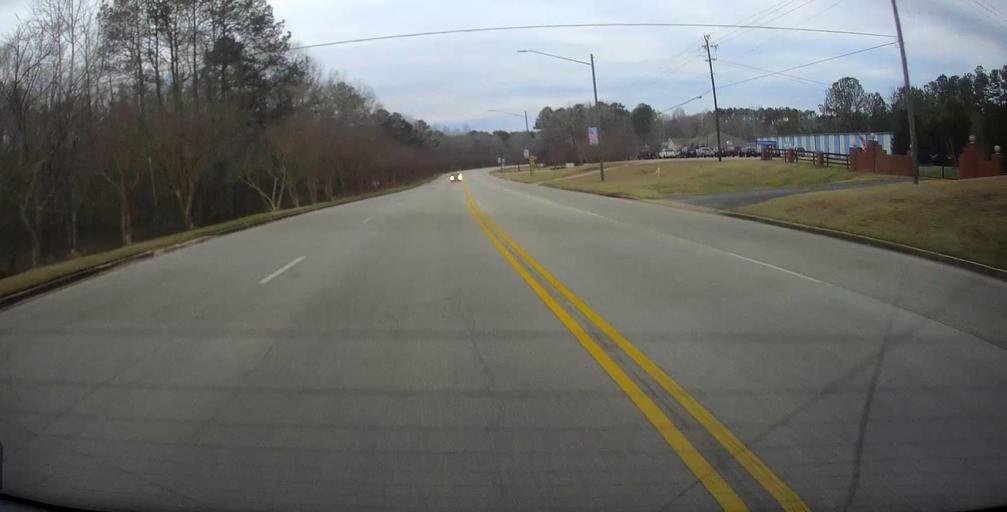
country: US
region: Alabama
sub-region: Chambers County
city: Valley
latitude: 32.8147
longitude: -85.1815
